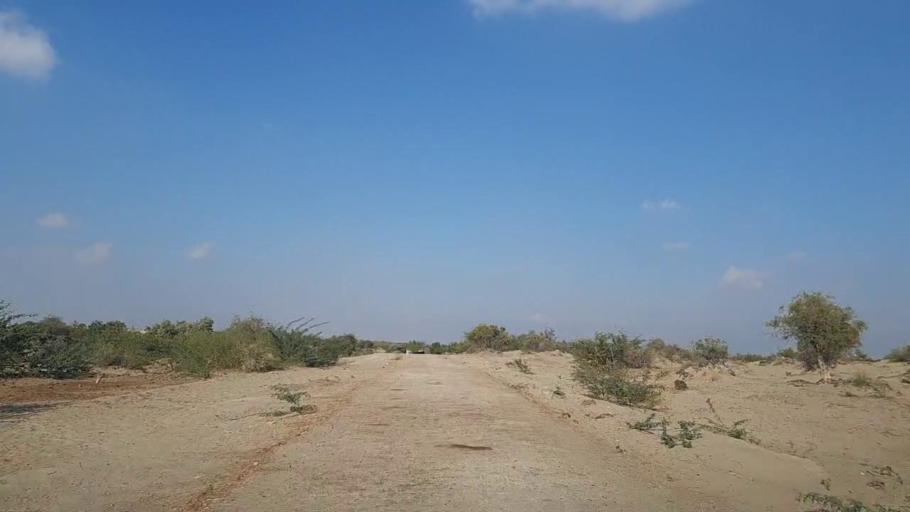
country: PK
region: Sindh
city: Tando Mittha Khan
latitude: 26.0181
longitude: 69.2502
